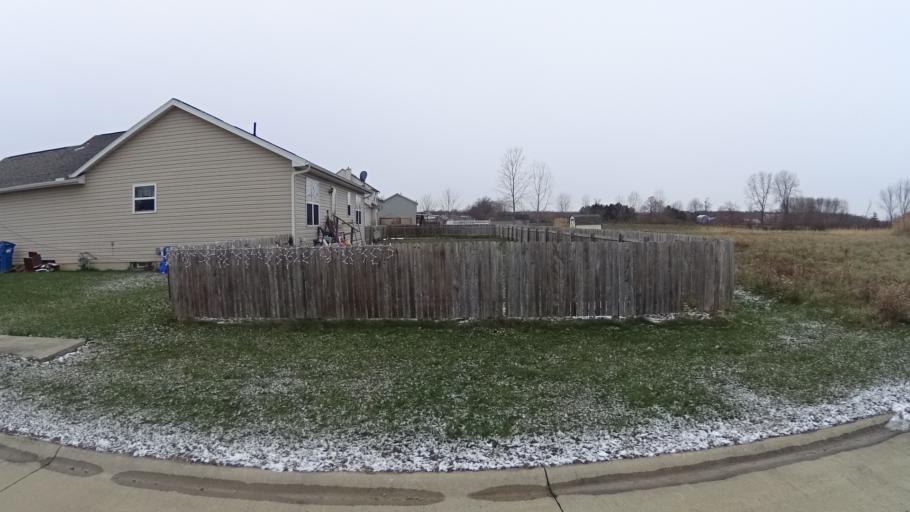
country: US
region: Ohio
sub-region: Lorain County
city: Lagrange
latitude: 41.2101
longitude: -82.1536
